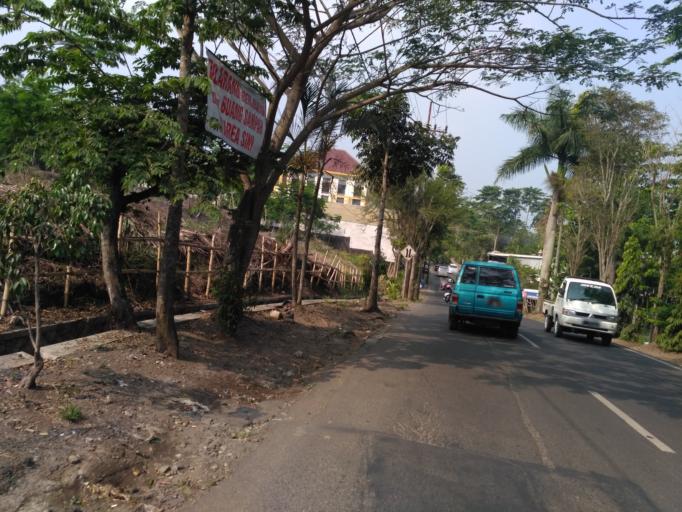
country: ID
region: East Java
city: Batu
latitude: -7.8632
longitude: 112.5300
